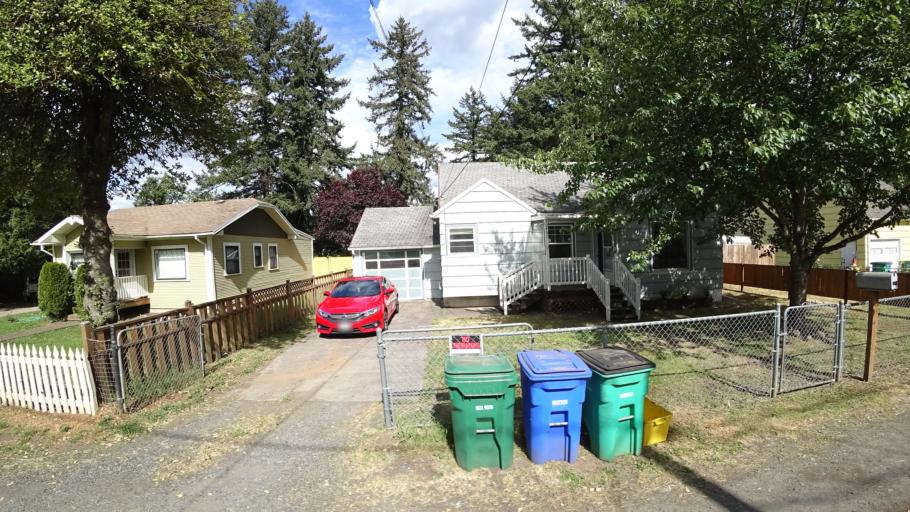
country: US
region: Oregon
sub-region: Multnomah County
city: Lents
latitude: 45.4957
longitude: -122.5405
